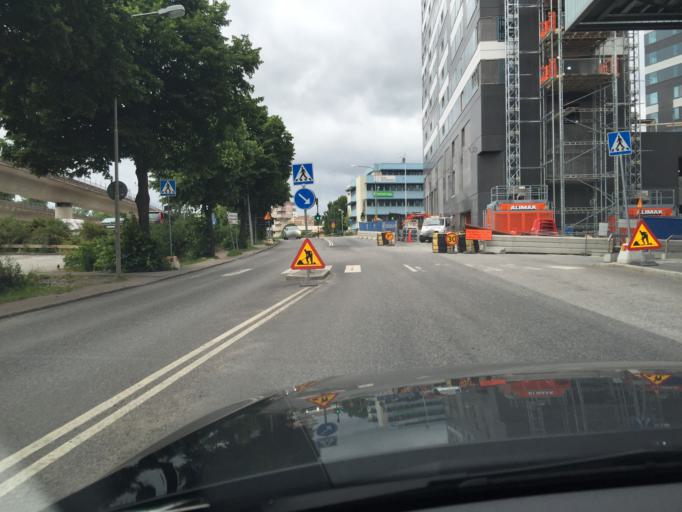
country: SE
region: Stockholm
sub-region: Stockholms Kommun
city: Kista
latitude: 59.4042
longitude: 17.9420
